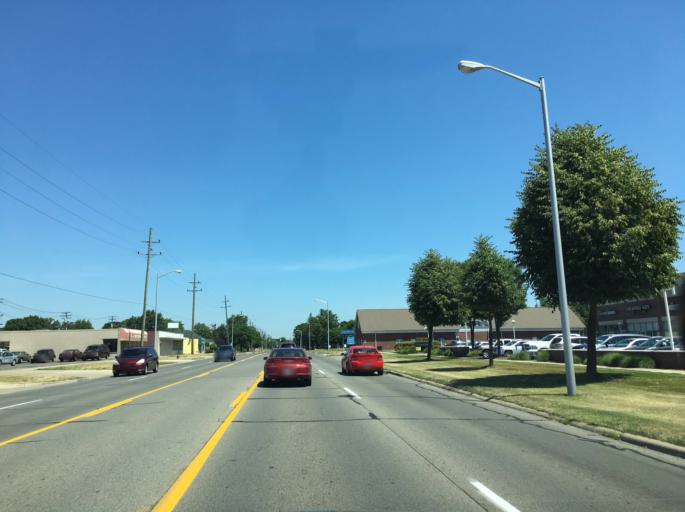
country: US
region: Michigan
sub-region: Macomb County
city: Saint Clair Shores
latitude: 42.5151
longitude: -82.8984
